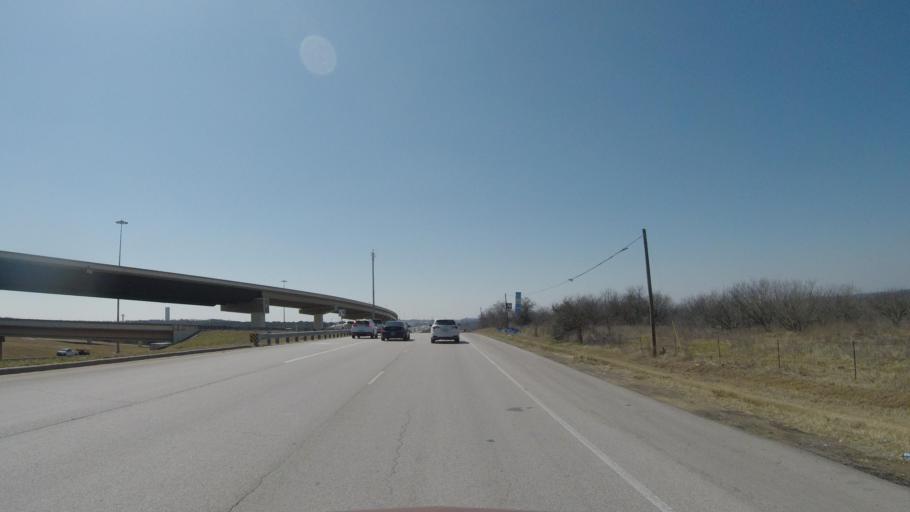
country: US
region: Texas
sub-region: Travis County
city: Onion Creek
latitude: 30.1120
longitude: -97.8081
